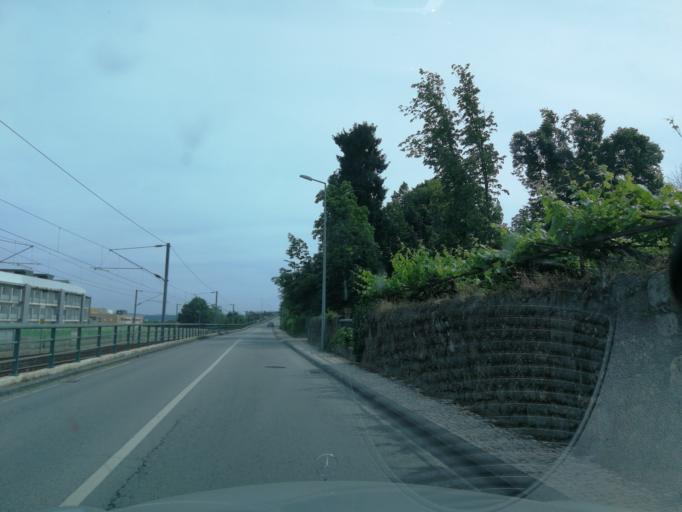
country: PT
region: Braga
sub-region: Vila Nova de Famalicao
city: Vila Nova de Famalicao
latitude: 41.4132
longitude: -8.5265
